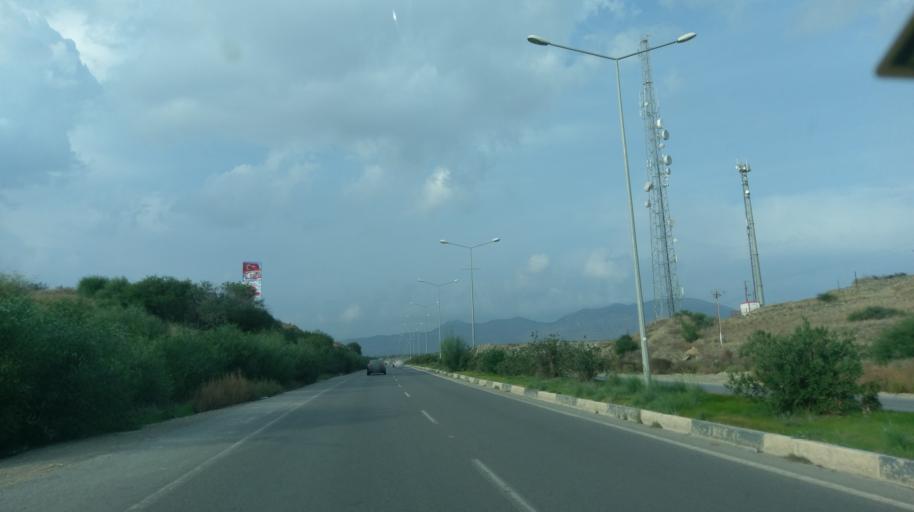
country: CY
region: Lefkosia
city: Nicosia
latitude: 35.2299
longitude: 33.3121
